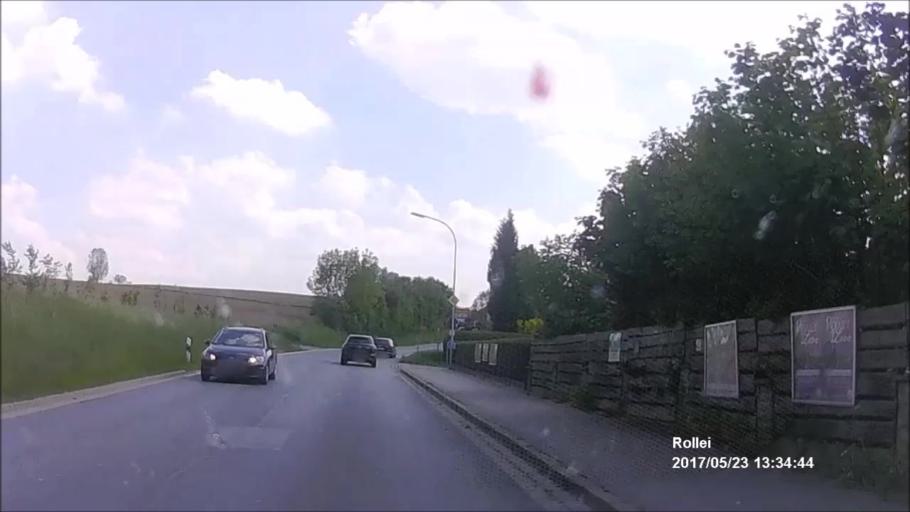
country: DE
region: Bavaria
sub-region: Upper Bavaria
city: Dorfen
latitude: 48.2636
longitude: 12.1570
